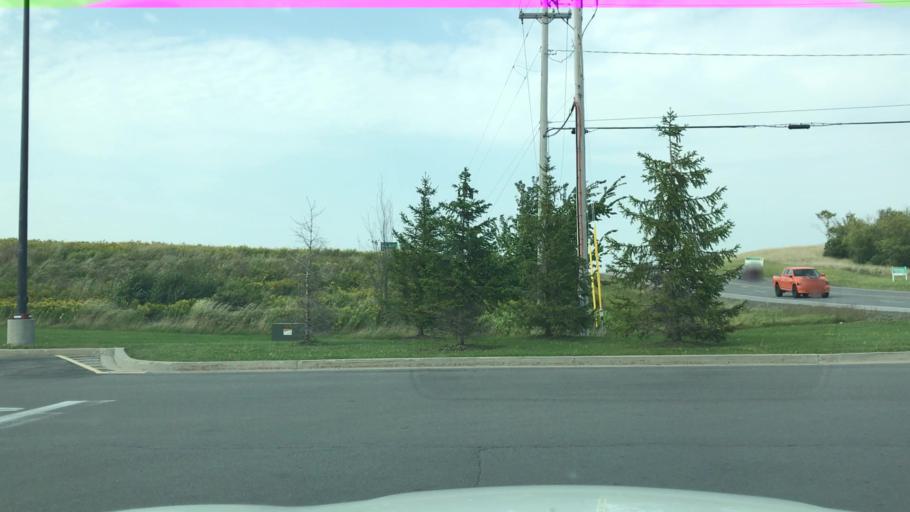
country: US
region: New York
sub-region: Jefferson County
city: Brownville
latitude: 43.9769
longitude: -75.9608
